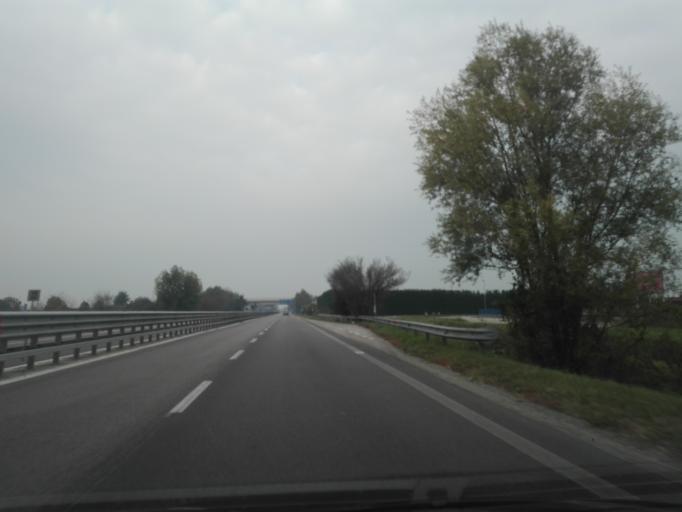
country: IT
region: Veneto
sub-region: Provincia di Verona
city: Spinimbecco
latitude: 45.1398
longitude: 11.3577
